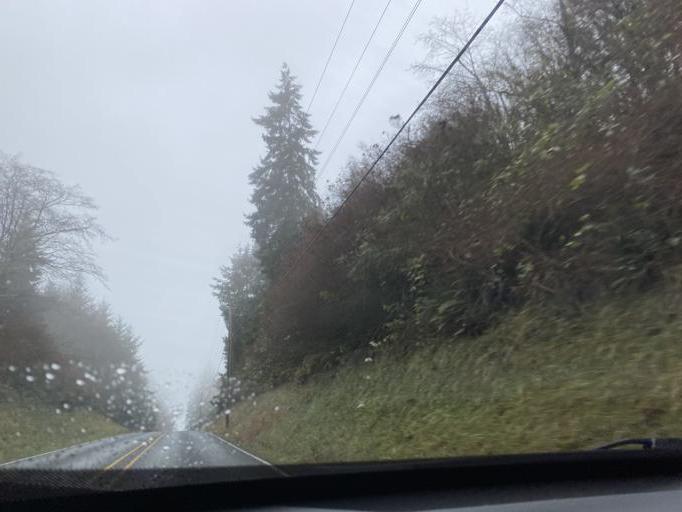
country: US
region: Washington
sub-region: Island County
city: Langley
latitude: 48.0771
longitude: -122.4745
